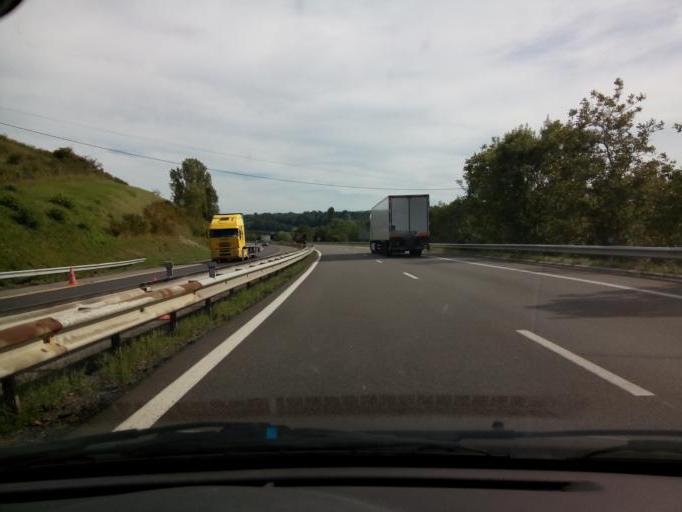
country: FR
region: Rhone-Alpes
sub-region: Departement de l'Isere
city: Cessieu
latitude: 45.5612
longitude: 5.3496
